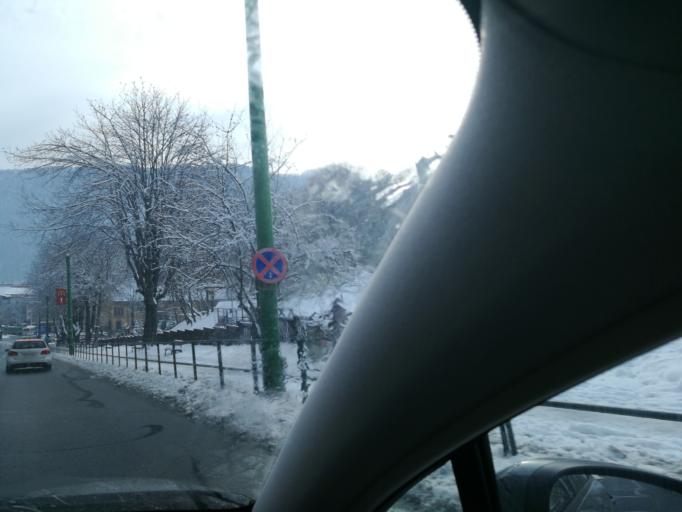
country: RO
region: Brasov
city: Brasov
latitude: 45.6470
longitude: 25.5857
